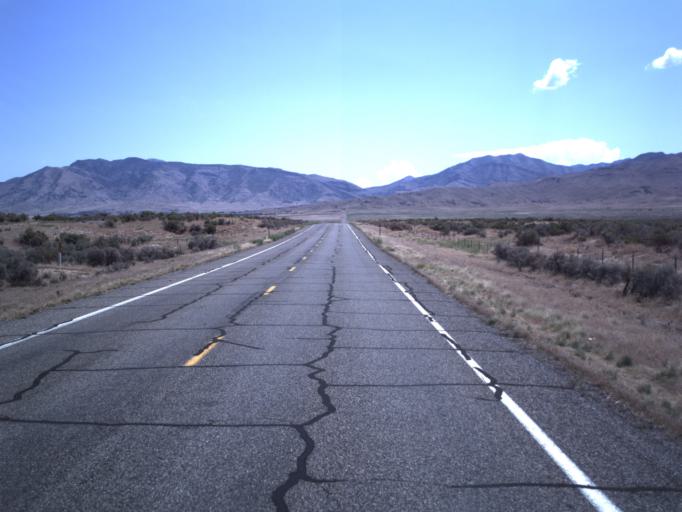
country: US
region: Utah
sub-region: Millard County
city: Delta
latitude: 39.3542
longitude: -112.4256
